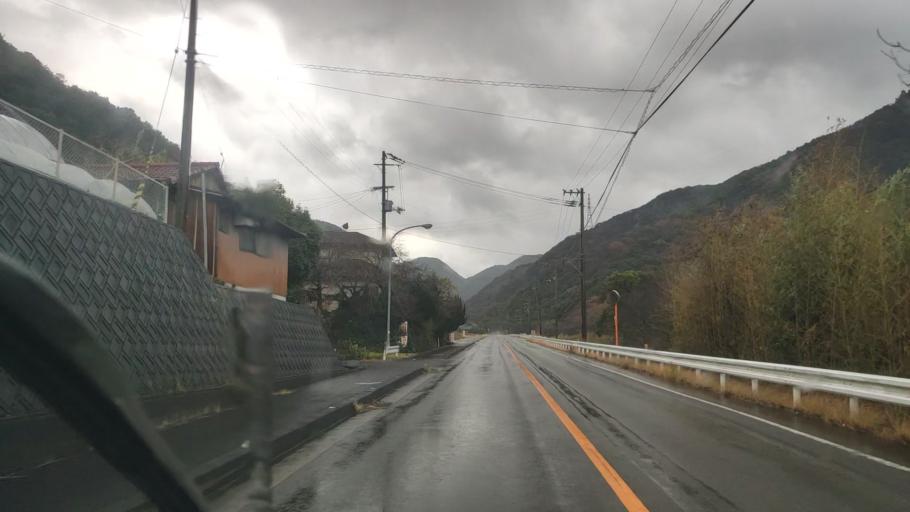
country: JP
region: Tokushima
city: Kamojimacho-jogejima
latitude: 34.1960
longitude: 134.3326
